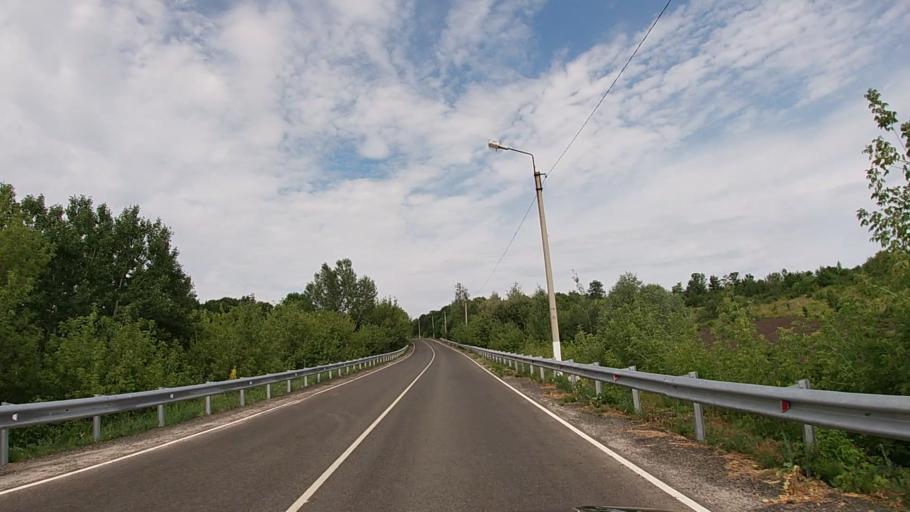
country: UA
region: Sumy
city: Krasnopillya
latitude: 50.8141
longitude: 35.4263
